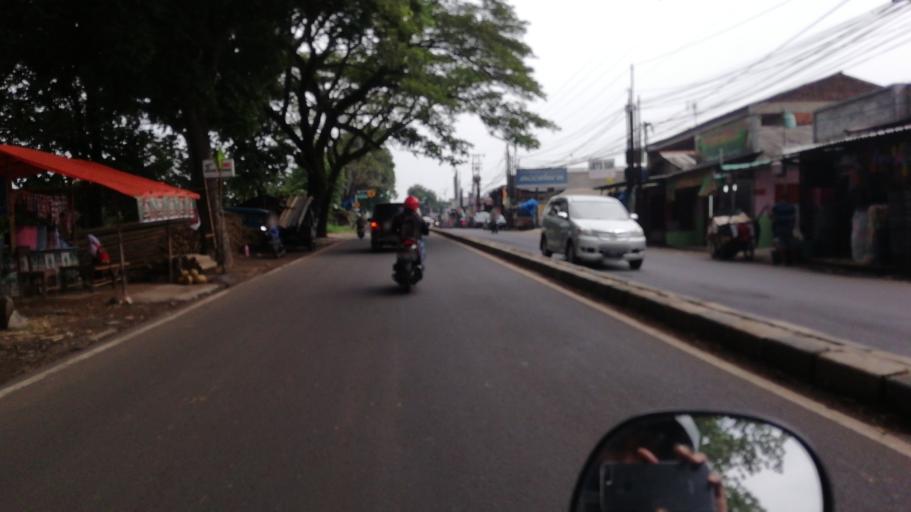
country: ID
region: West Java
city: Cibinong
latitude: -6.4520
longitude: 106.8539
